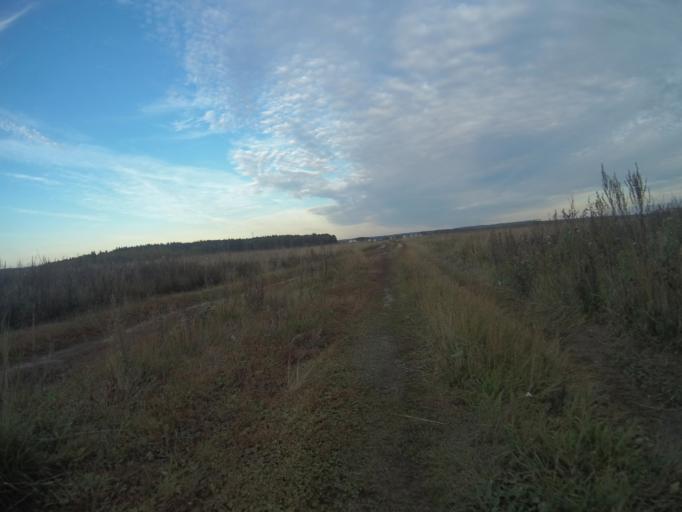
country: RU
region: Vladimir
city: Raduzhnyy
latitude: 56.0169
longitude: 40.3672
